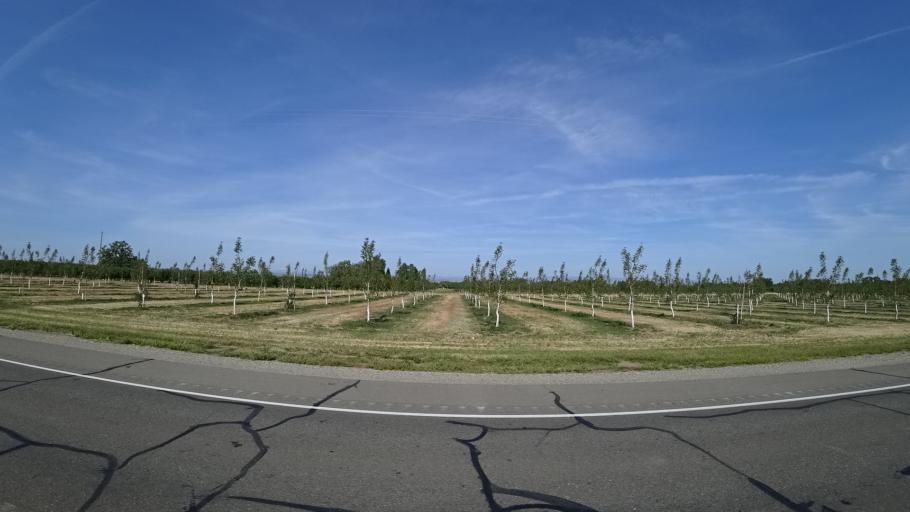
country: US
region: California
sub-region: Tehama County
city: Los Molinos
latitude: 39.9994
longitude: -122.0890
